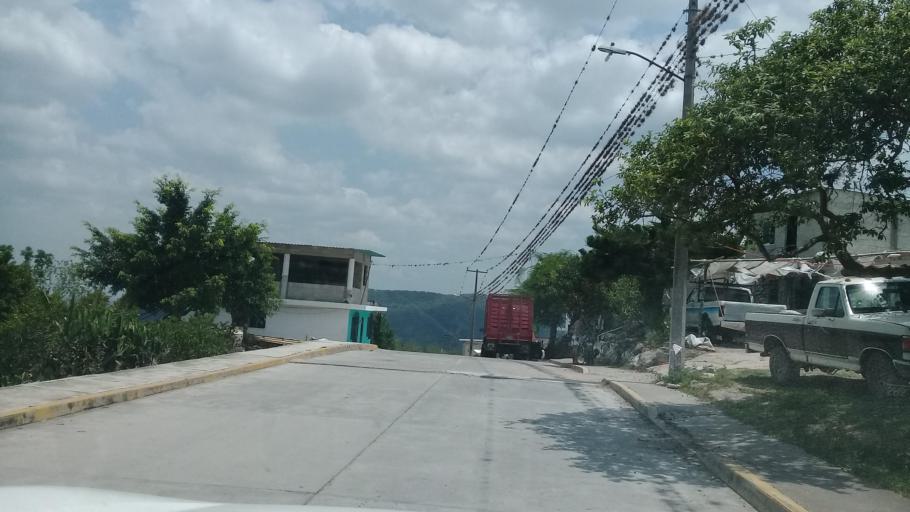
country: MX
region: Veracruz
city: Jalcomulco
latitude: 19.3946
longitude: -96.7890
